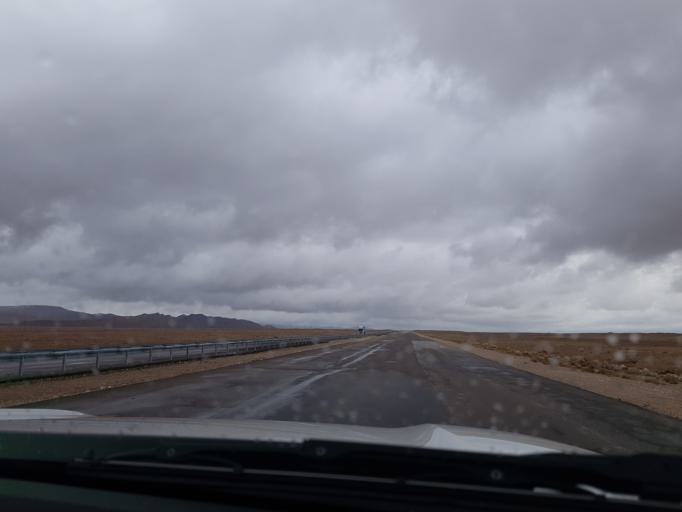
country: TM
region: Balkan
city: Balkanabat
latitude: 39.9104
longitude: 53.9240
